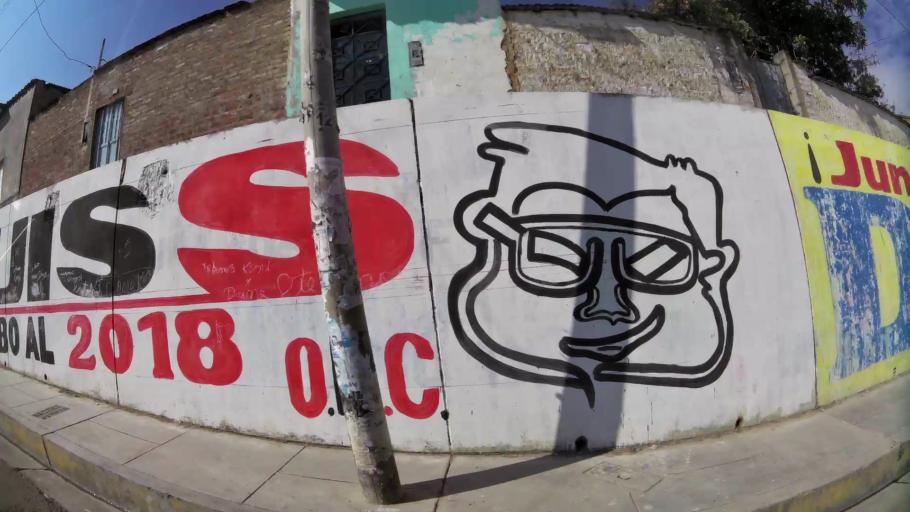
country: PE
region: Junin
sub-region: Provincia de Huancayo
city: Huancayo
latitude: -12.0586
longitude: -75.1962
